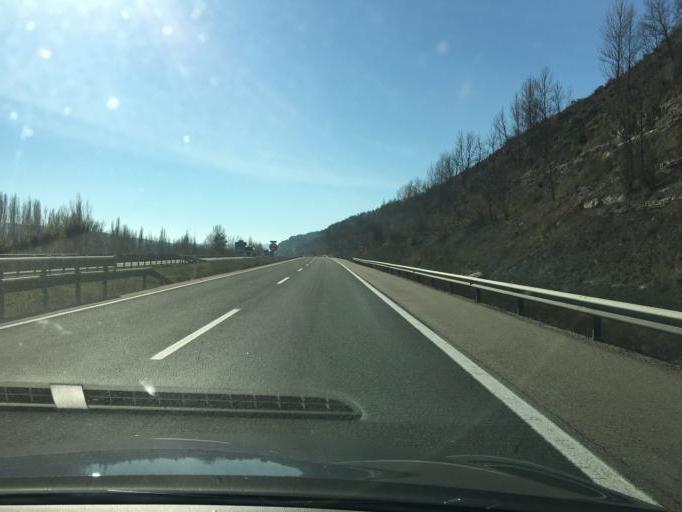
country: ES
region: Castille and Leon
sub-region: Provincia de Burgos
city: Pradanos de Bureba
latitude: 42.5228
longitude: -3.3384
